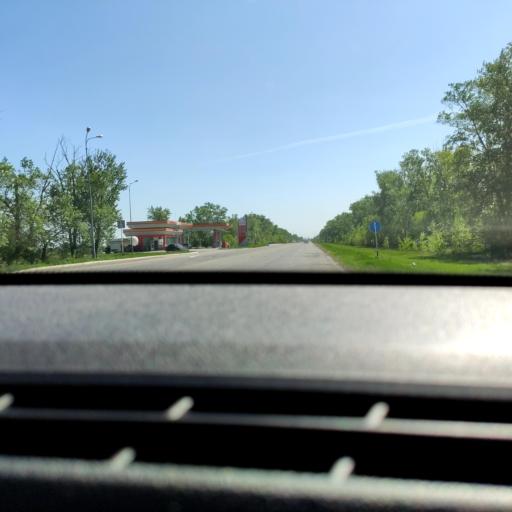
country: RU
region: Samara
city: Tol'yatti
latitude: 53.5975
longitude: 49.4081
